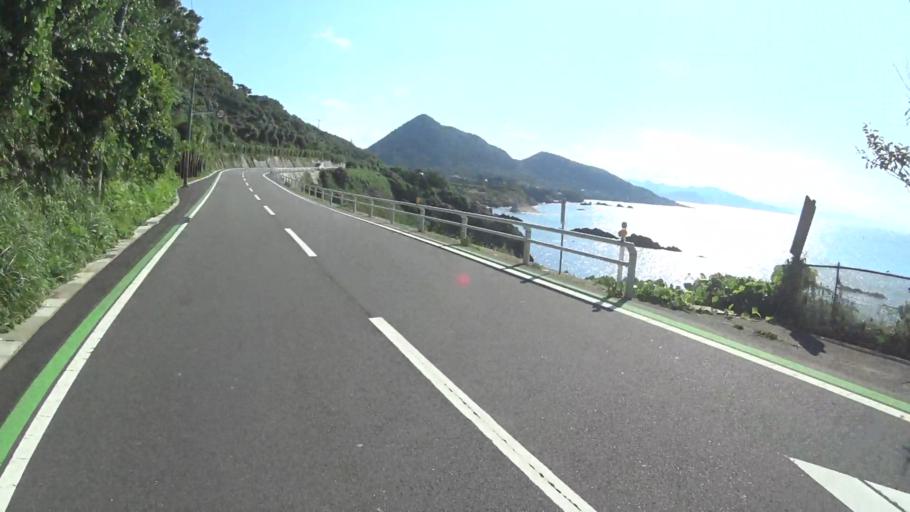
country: JP
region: Kyoto
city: Miyazu
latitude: 35.7288
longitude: 135.0873
